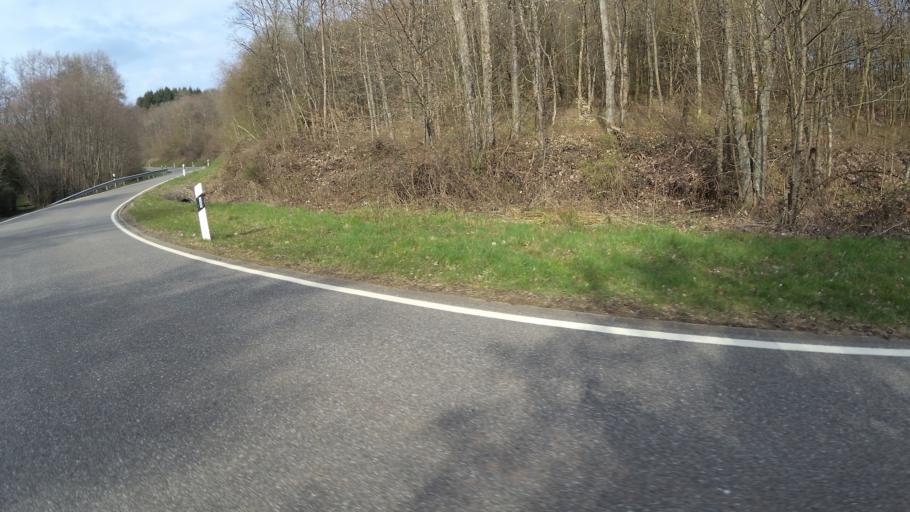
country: DE
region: Rheinland-Pfalz
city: Reichweiler
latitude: 49.5463
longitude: 7.2864
